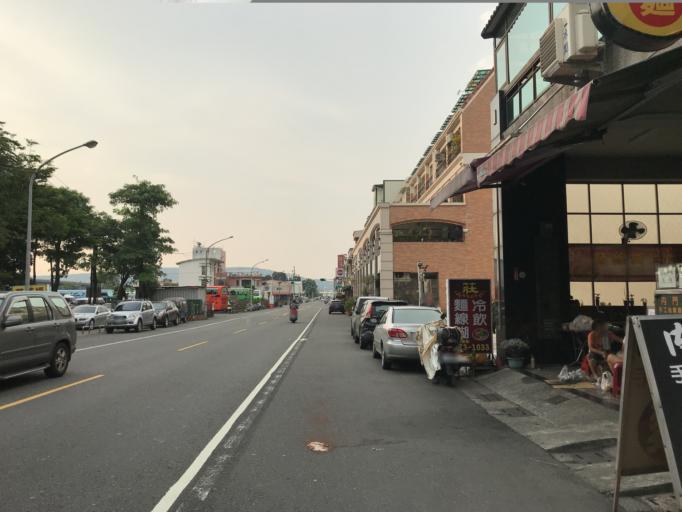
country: TW
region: Taiwan
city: Fengshan
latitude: 22.6766
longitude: 120.3315
